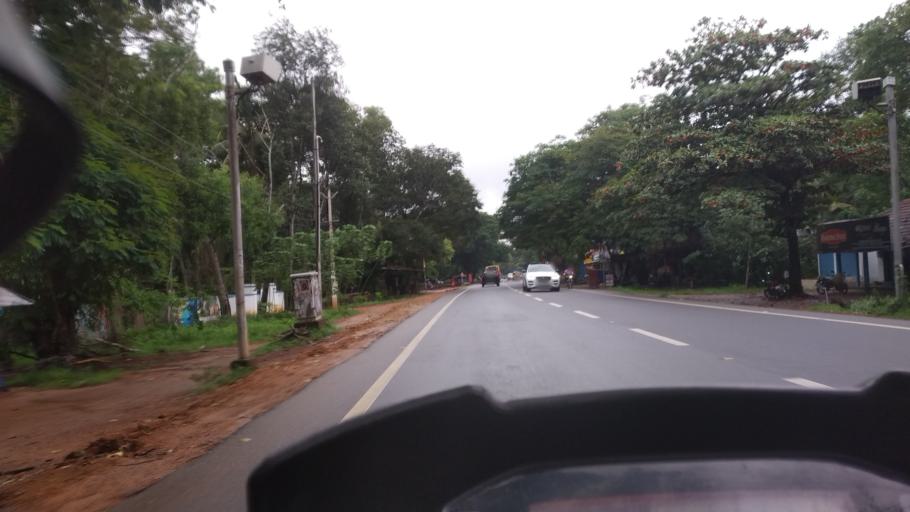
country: IN
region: Kerala
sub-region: Alappuzha
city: Mavelikara
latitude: 9.3009
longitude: 76.4331
